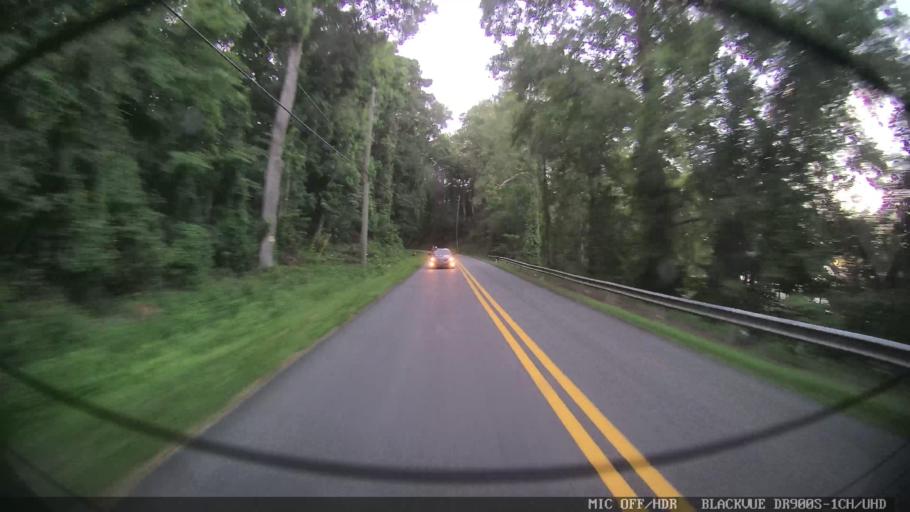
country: US
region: Georgia
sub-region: Bartow County
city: Emerson
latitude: 34.0954
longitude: -84.7235
